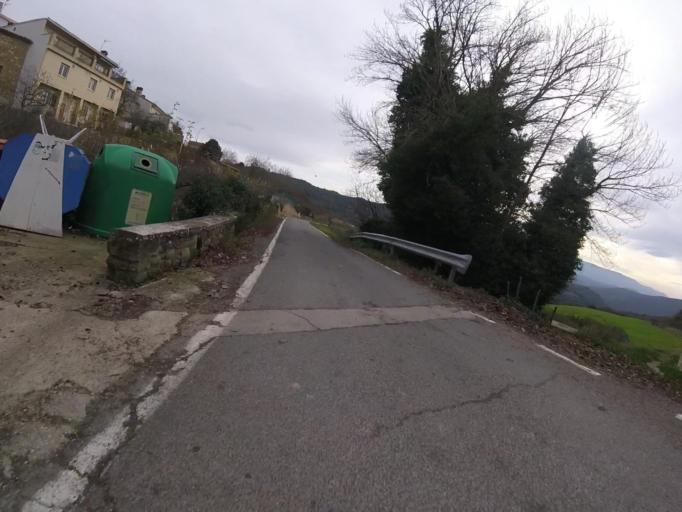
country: ES
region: Navarre
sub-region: Provincia de Navarra
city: Estella
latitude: 42.7164
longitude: -2.0505
